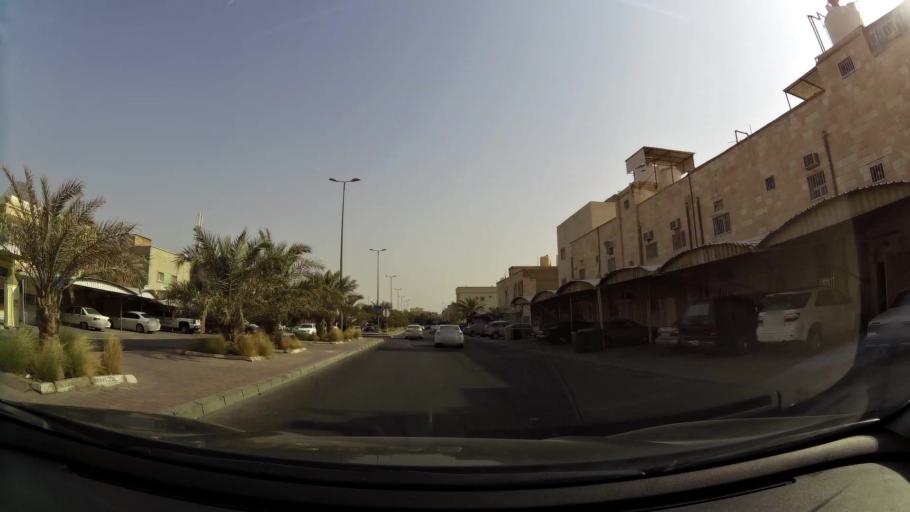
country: KW
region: Muhafazat al Jahra'
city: Al Jahra'
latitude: 29.3510
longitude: 47.6807
